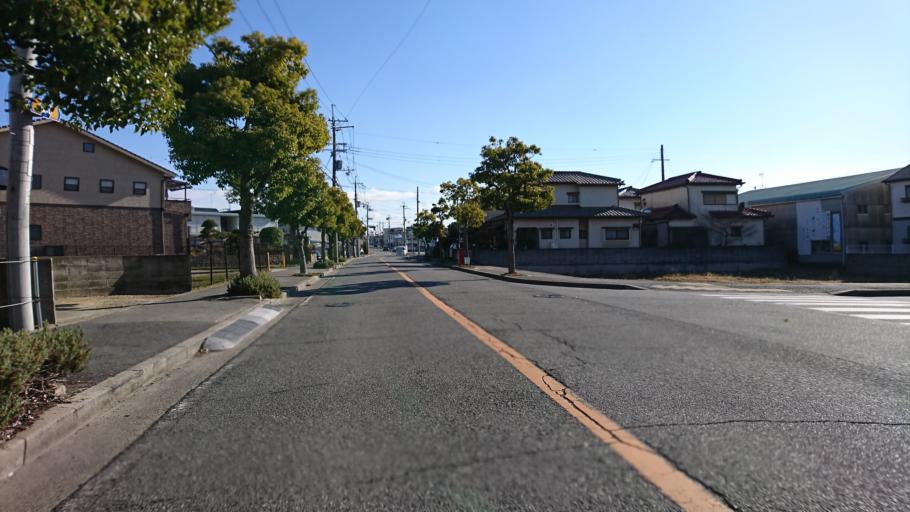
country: JP
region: Hyogo
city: Kakogawacho-honmachi
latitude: 34.7238
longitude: 134.8774
